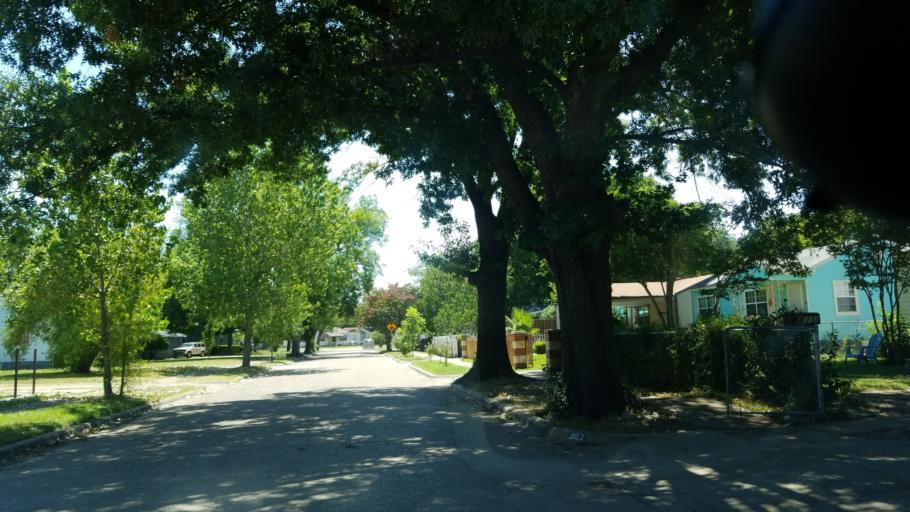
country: US
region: Texas
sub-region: Dallas County
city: Cockrell Hill
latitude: 32.7162
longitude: -96.8519
